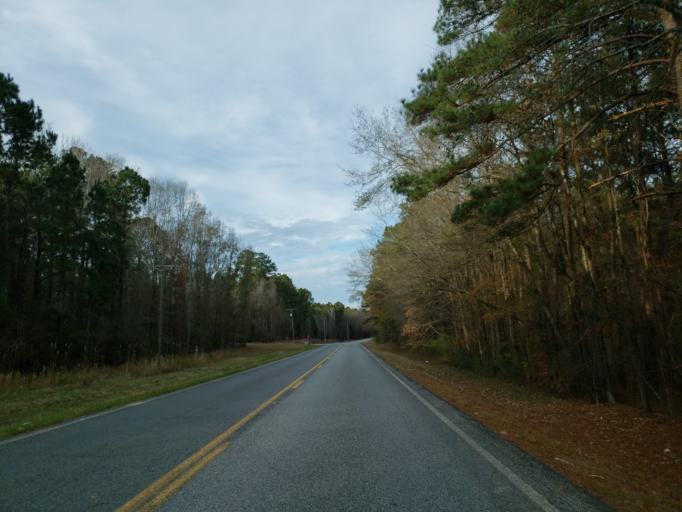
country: US
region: Mississippi
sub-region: Wayne County
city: Waynesboro
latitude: 31.8367
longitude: -88.6893
